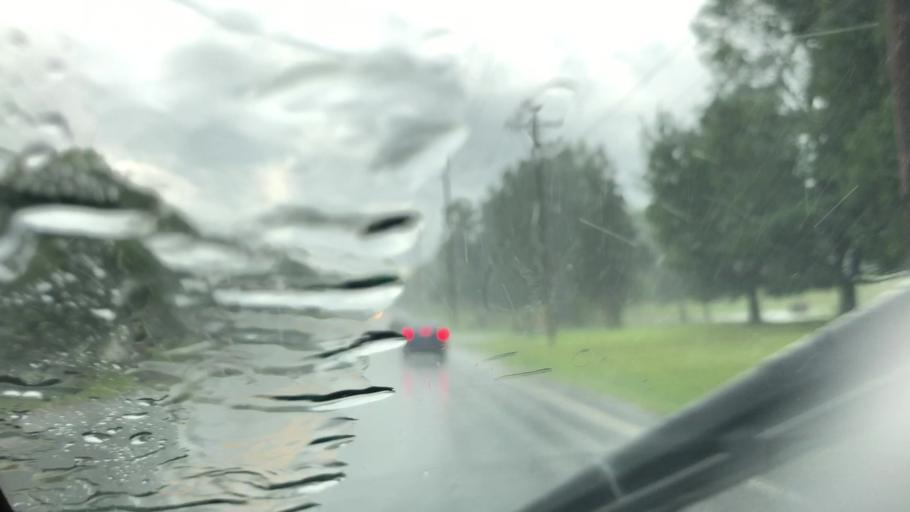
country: US
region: Ohio
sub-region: Stark County
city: Massillon
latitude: 40.8353
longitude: -81.5022
